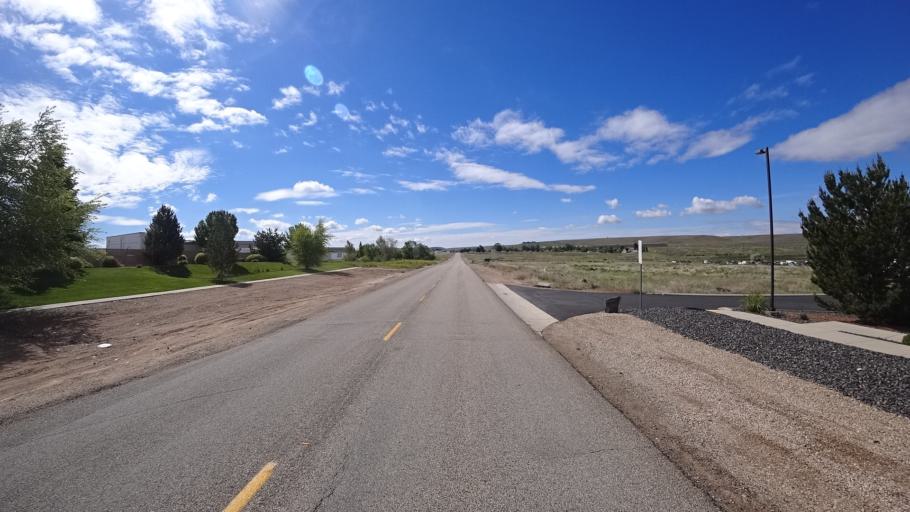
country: US
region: Idaho
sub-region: Ada County
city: Boise
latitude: 43.5338
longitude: -116.1597
